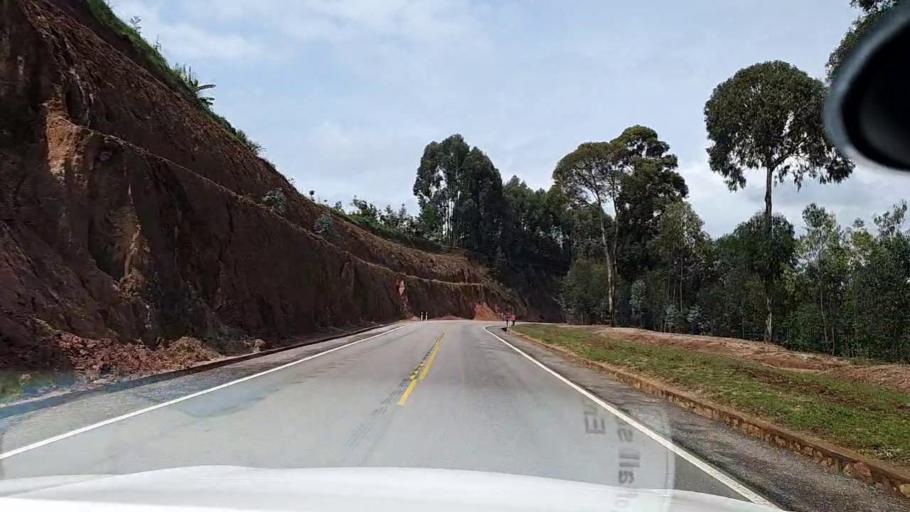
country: RW
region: Southern Province
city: Nzega
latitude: -2.4927
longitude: 29.5097
